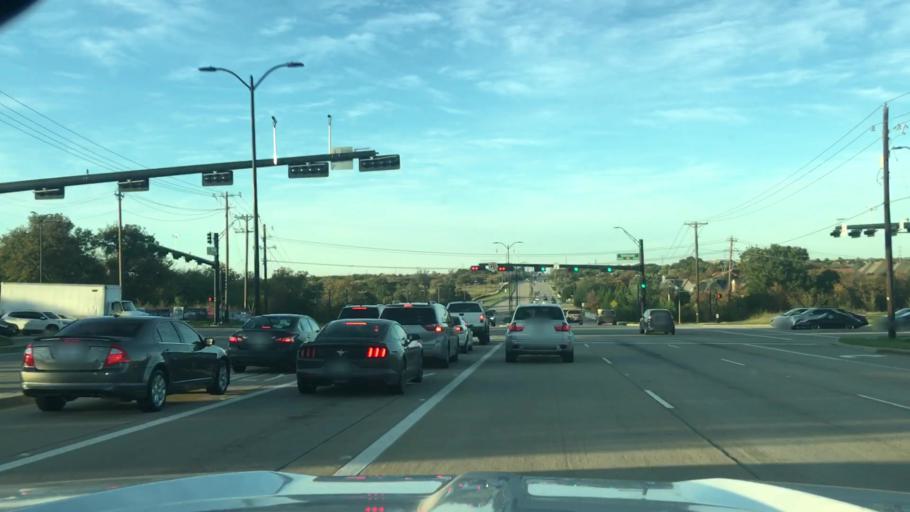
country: US
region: Texas
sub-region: Collin County
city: Frisco
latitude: 33.1740
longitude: -96.8030
